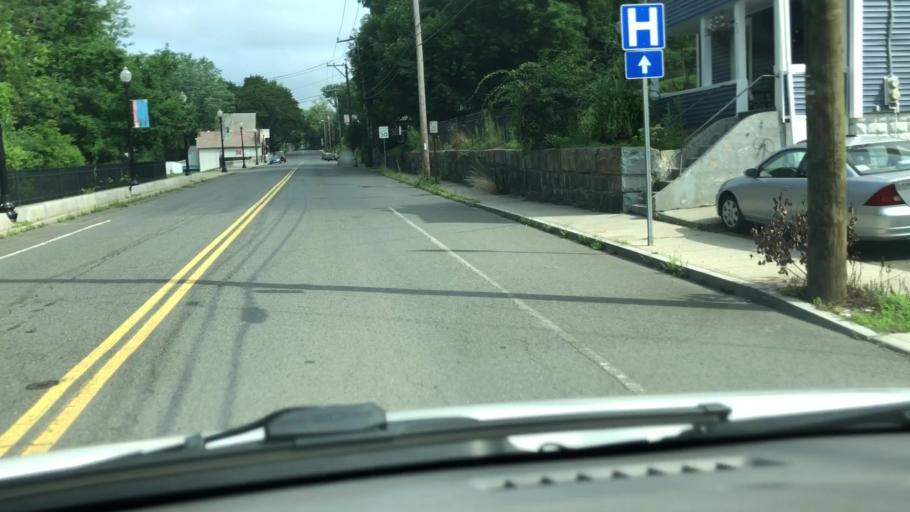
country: US
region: Massachusetts
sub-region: Franklin County
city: Greenfield
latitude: 42.5806
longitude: -72.5992
